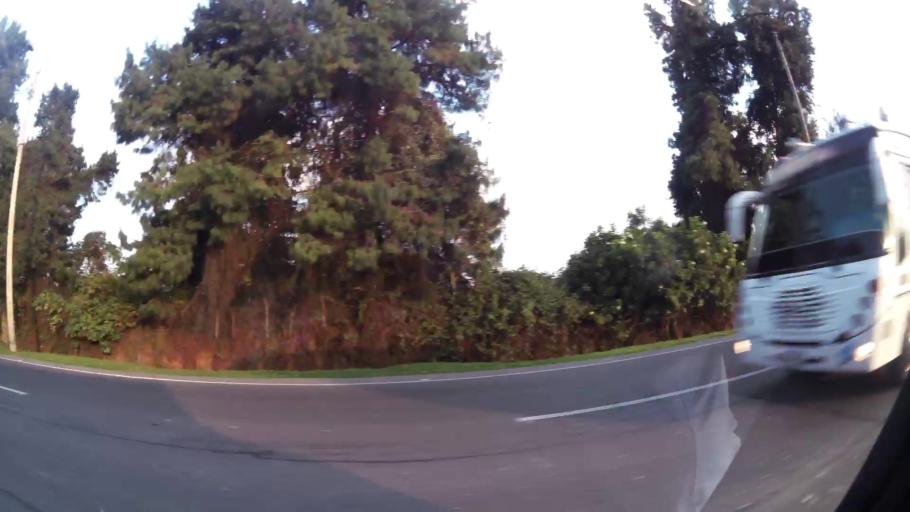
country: CO
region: Cundinamarca
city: Cota
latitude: 4.7978
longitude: -74.1119
